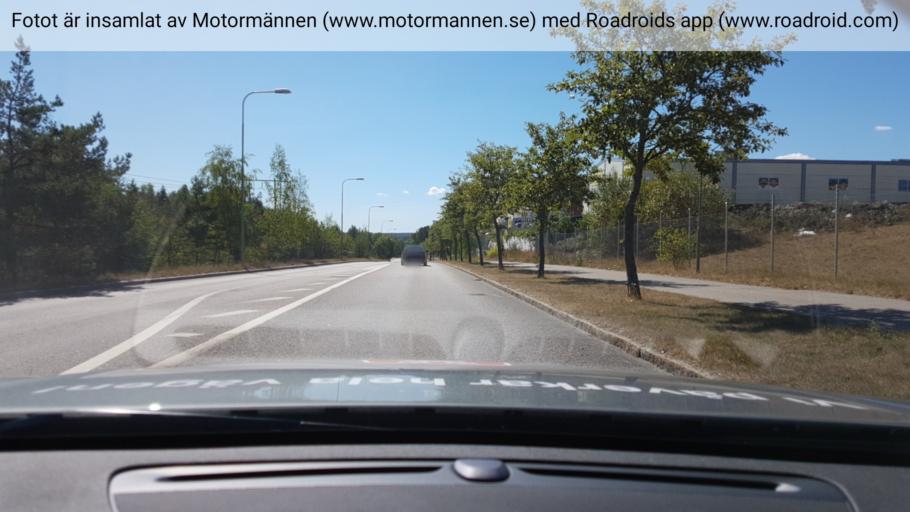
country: SE
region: Stockholm
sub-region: Nacka Kommun
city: Alta
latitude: 59.2396
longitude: 18.1950
